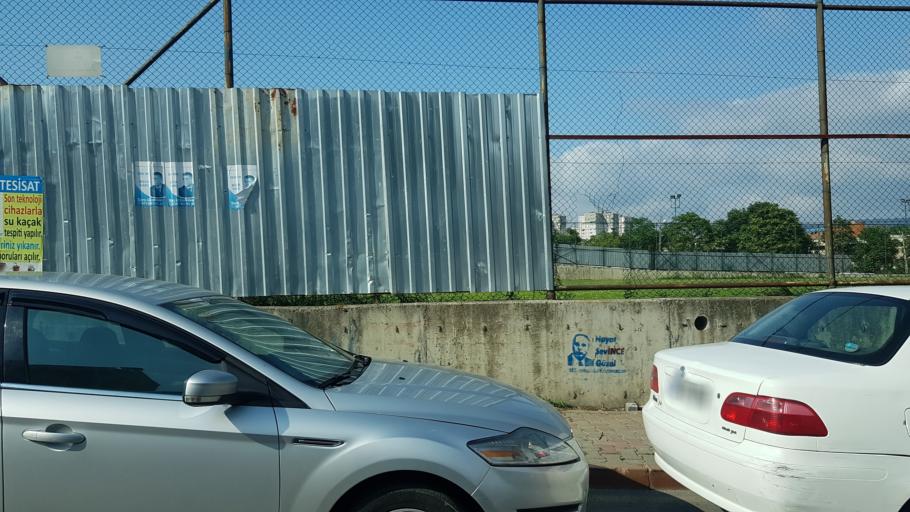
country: TR
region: Istanbul
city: Maltepe
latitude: 40.9004
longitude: 29.1960
